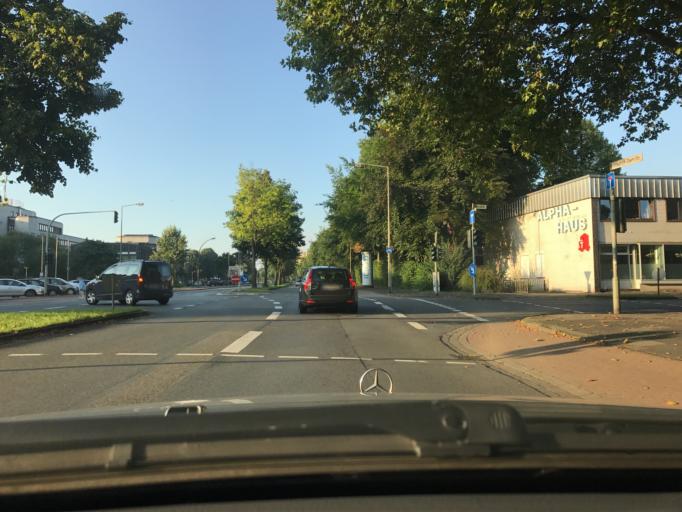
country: DE
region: North Rhine-Westphalia
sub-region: Regierungsbezirk Dusseldorf
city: Hochfeld
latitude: 51.4034
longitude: 6.7109
